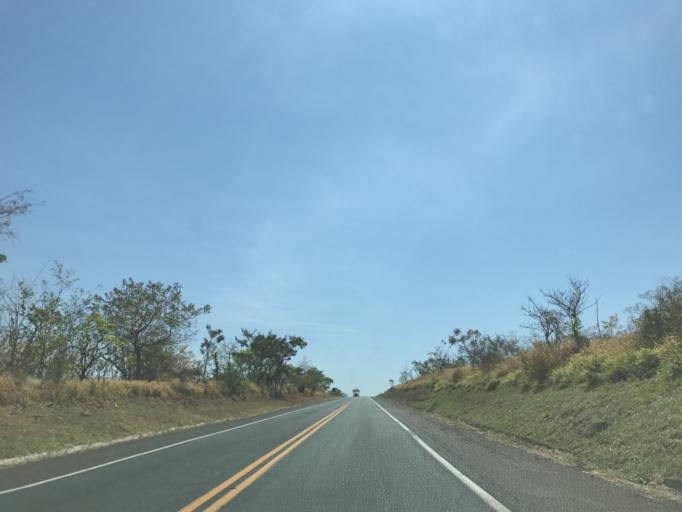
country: BR
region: Minas Gerais
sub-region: Prata
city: Prata
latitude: -19.5175
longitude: -48.8368
